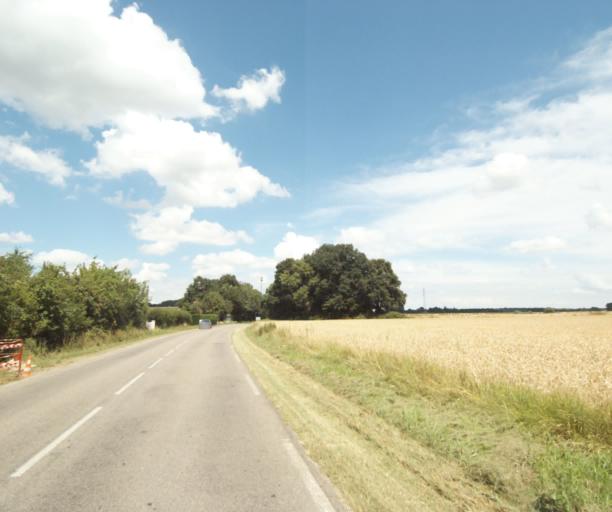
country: FR
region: Ile-de-France
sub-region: Departement de Seine-et-Marne
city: Vulaines-sur-Seine
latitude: 48.4356
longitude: 2.7714
